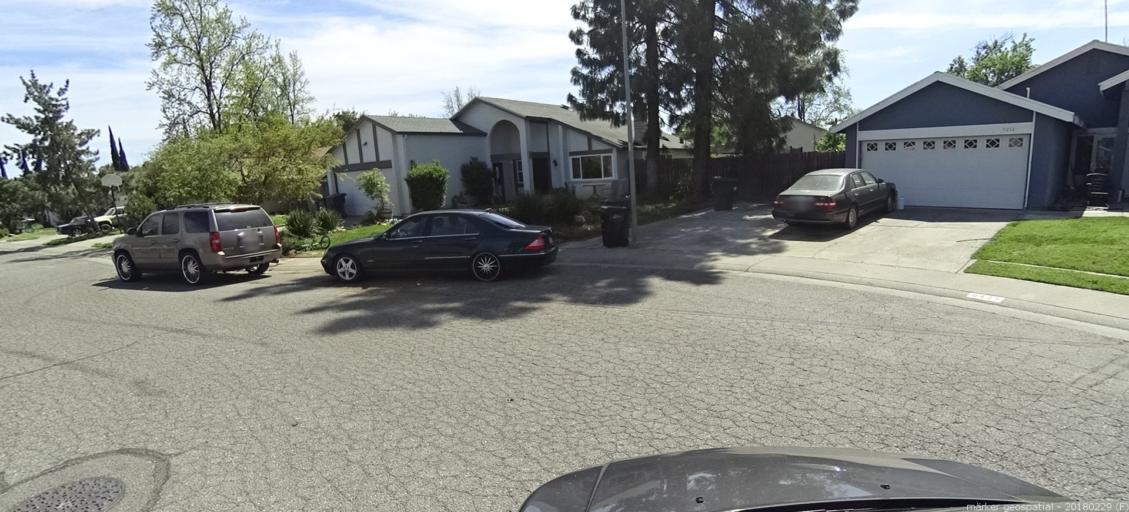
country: US
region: California
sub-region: Sacramento County
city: Rosemont
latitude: 38.5495
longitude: -121.3471
